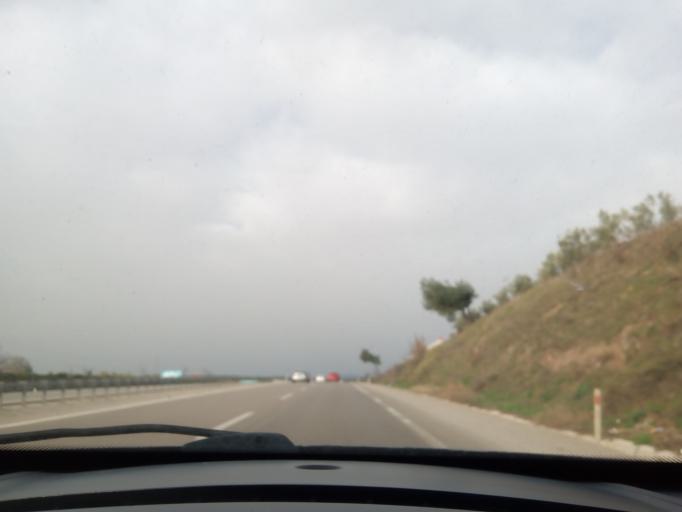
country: TR
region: Bursa
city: Mahmudiye
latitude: 40.2148
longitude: 28.6663
